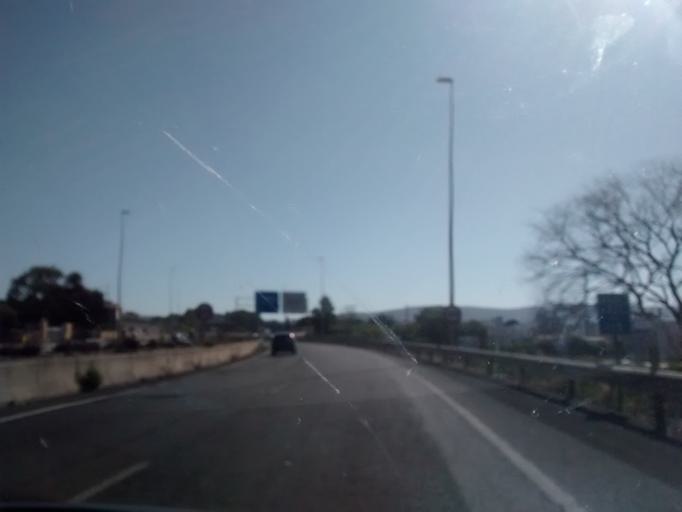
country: ES
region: Andalusia
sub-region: Provincia de Cadiz
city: San Roque
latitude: 36.2038
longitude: -5.4181
